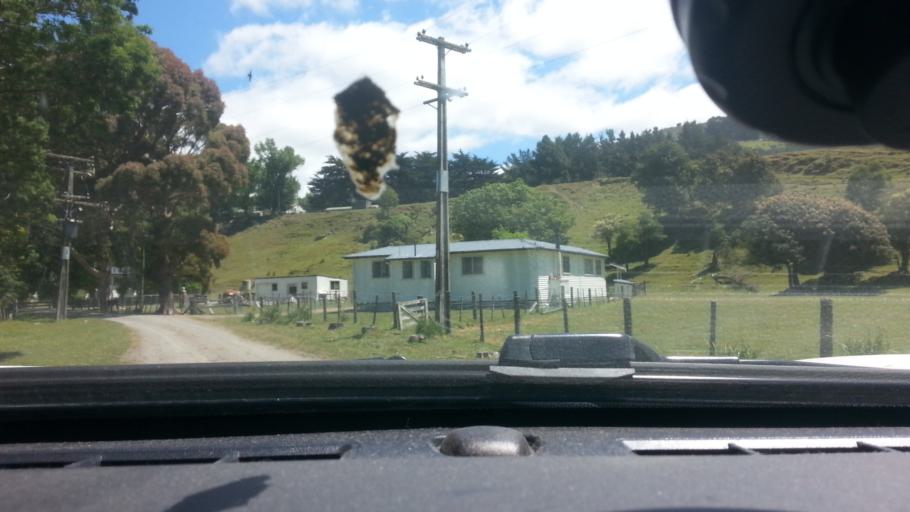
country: NZ
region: Wellington
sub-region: South Wairarapa District
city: Waipawa
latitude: -41.3810
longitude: 175.4536
